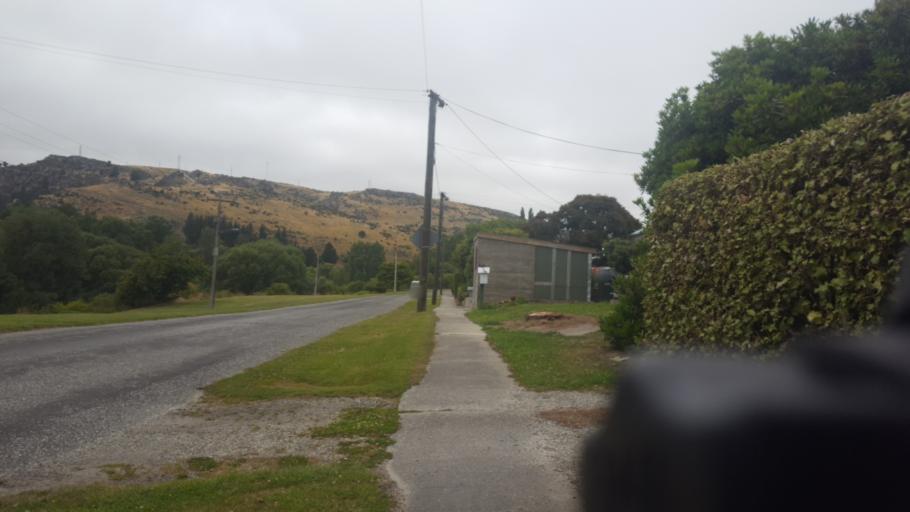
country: NZ
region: Otago
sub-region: Queenstown-Lakes District
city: Kingston
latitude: -45.5386
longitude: 169.3139
